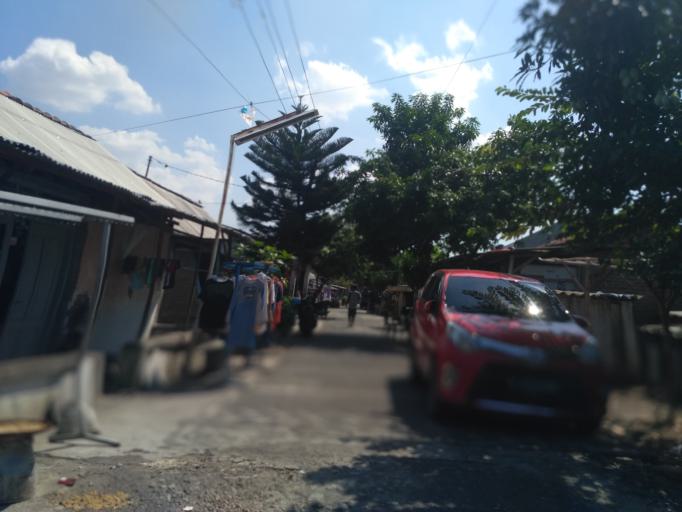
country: ID
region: Central Java
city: Semarang
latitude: -7.0000
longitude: 110.4413
